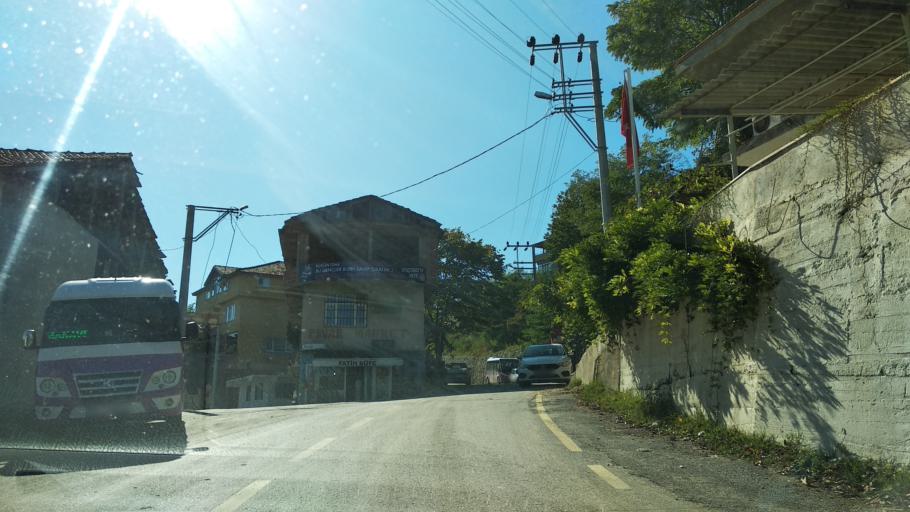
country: TR
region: Sakarya
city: Karasu
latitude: 41.1034
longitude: 30.6342
